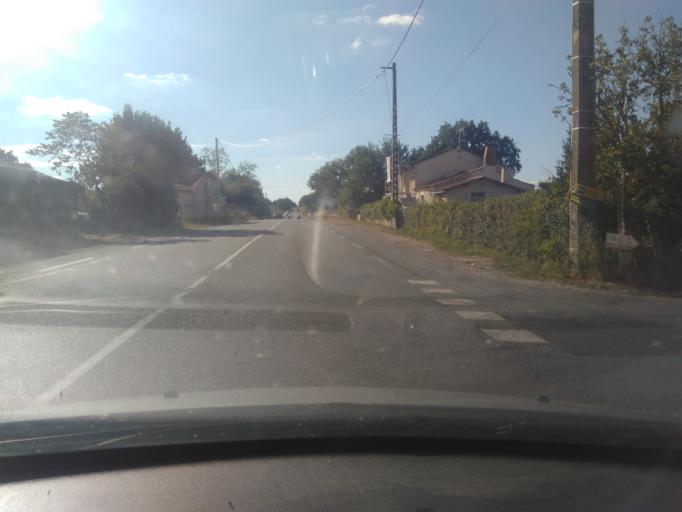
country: FR
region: Pays de la Loire
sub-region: Departement de la Vendee
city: Saint-Florent-des-Bois
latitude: 46.6003
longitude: -1.3275
